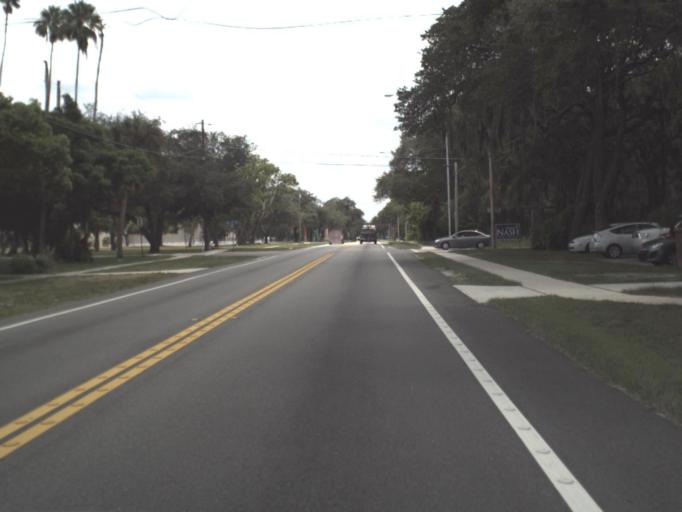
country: US
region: Florida
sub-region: Hillsborough County
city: Wimauma
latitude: 27.7125
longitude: -82.3167
